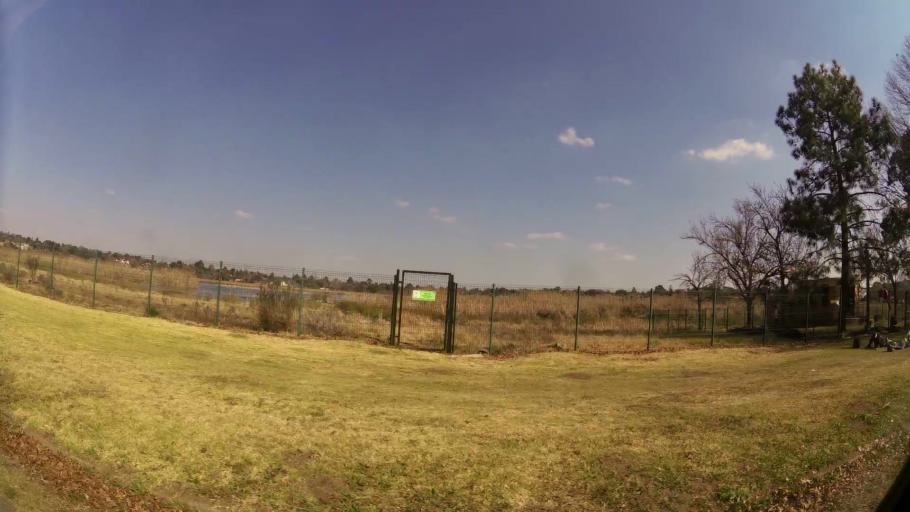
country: ZA
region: Gauteng
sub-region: Ekurhuleni Metropolitan Municipality
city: Benoni
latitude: -26.1901
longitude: 28.2956
